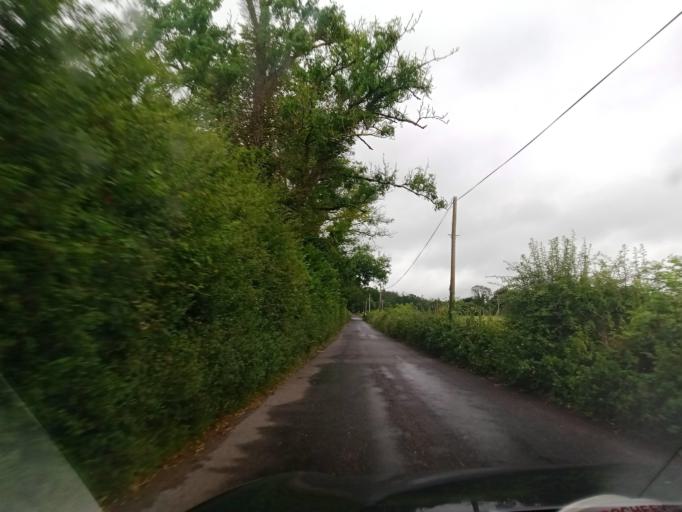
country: IE
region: Leinster
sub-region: Laois
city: Abbeyleix
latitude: 52.9295
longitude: -7.2779
